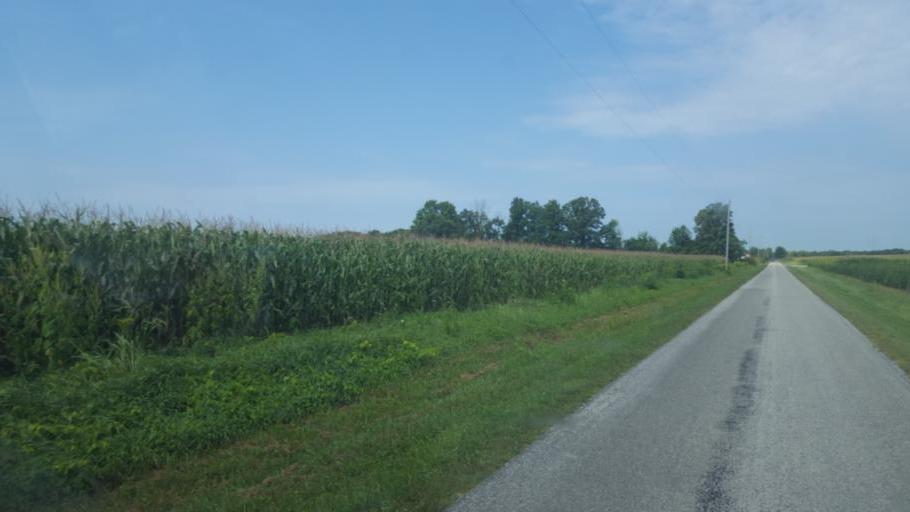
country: US
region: Ohio
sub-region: Delaware County
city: Ashley
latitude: 40.4415
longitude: -83.0229
